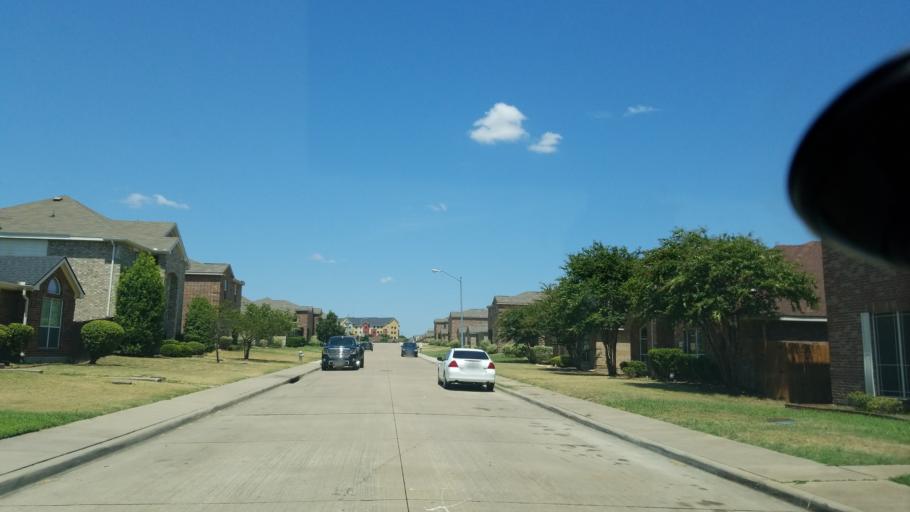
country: US
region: Texas
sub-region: Dallas County
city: Duncanville
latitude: 32.6407
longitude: -96.8841
